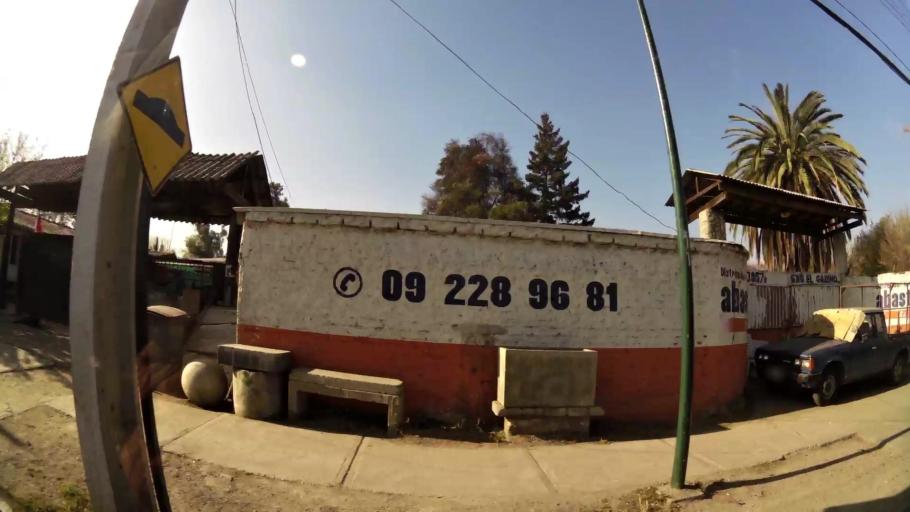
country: CL
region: Santiago Metropolitan
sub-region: Provincia de Santiago
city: Villa Presidente Frei, Nunoa, Santiago, Chile
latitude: -33.3534
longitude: -70.5090
